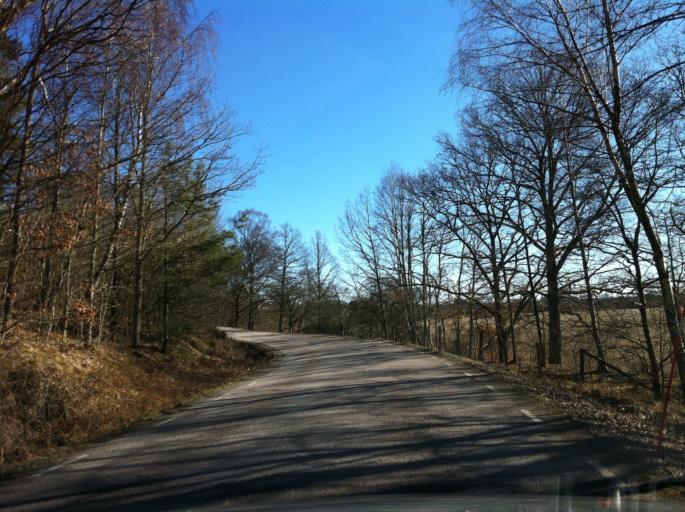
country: SE
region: Vaestra Goetaland
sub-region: Vanersborgs Kommun
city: Vargon
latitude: 58.3695
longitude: 12.4855
